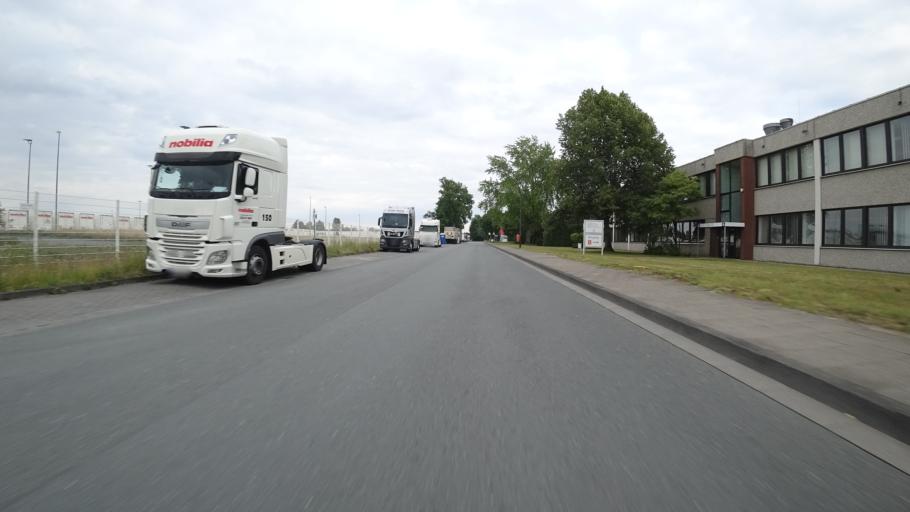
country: DE
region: North Rhine-Westphalia
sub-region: Regierungsbezirk Detmold
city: Verl
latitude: 51.8834
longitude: 8.4508
